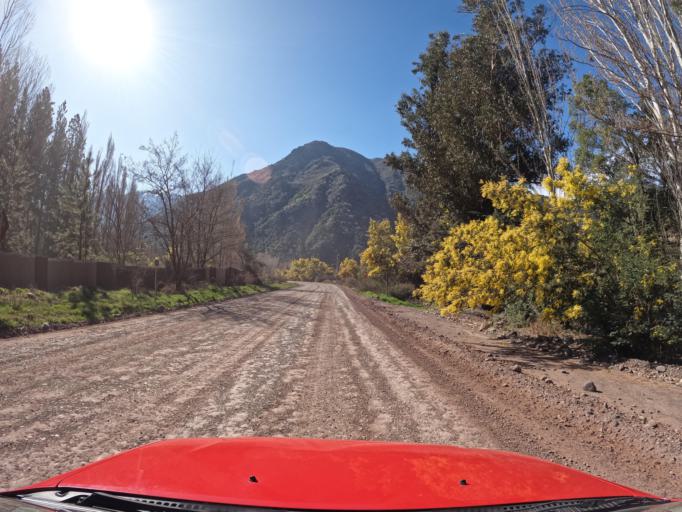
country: CL
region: O'Higgins
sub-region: Provincia de Colchagua
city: Chimbarongo
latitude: -35.0116
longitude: -70.7470
